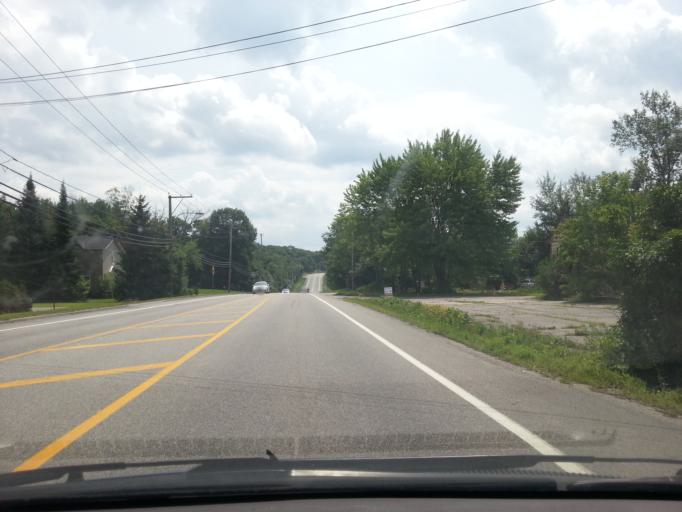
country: CA
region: Quebec
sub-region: Outaouais
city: Gatineau
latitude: 45.5209
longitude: -75.7722
